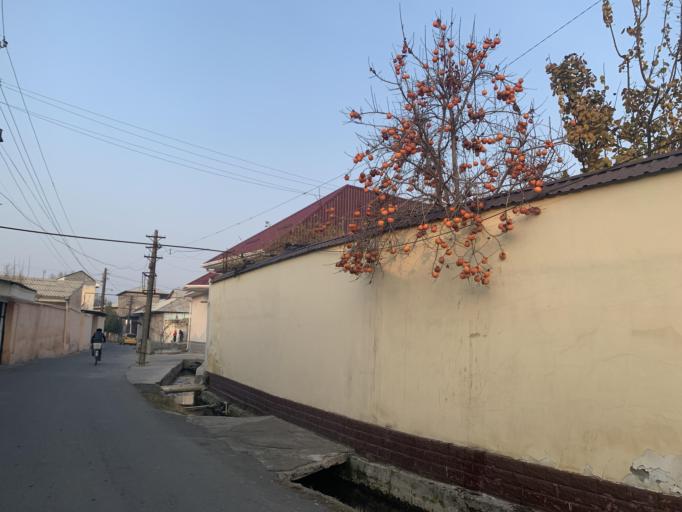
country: UZ
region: Fergana
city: Qo`qon
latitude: 40.5337
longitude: 70.9308
